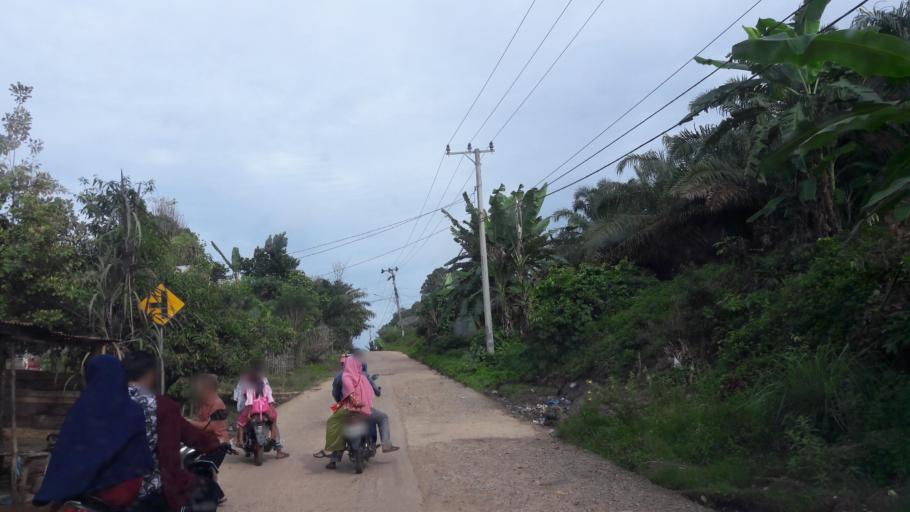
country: ID
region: South Sumatra
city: Gunungmegang Dalam
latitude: -3.2858
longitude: 103.7273
